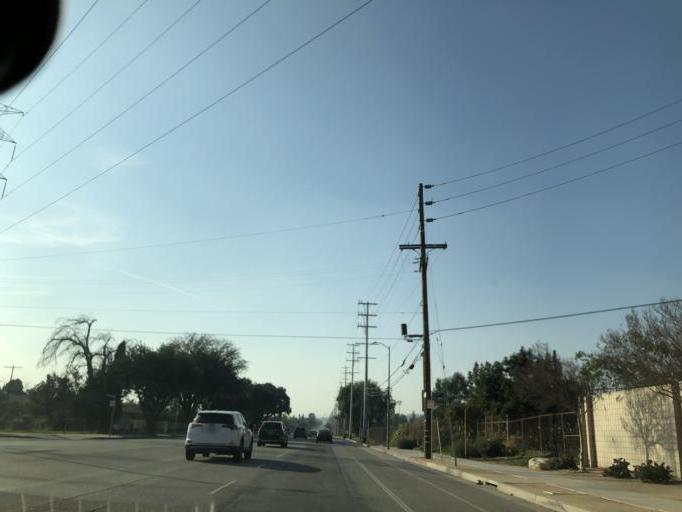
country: US
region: California
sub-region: Los Angeles County
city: San Fernando
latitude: 34.2792
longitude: -118.4799
